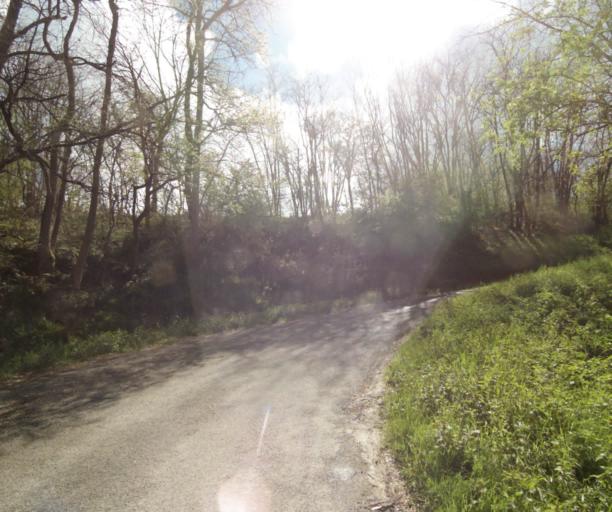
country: FR
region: Midi-Pyrenees
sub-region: Departement de l'Ariege
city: Saverdun
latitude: 43.2030
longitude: 1.5845
